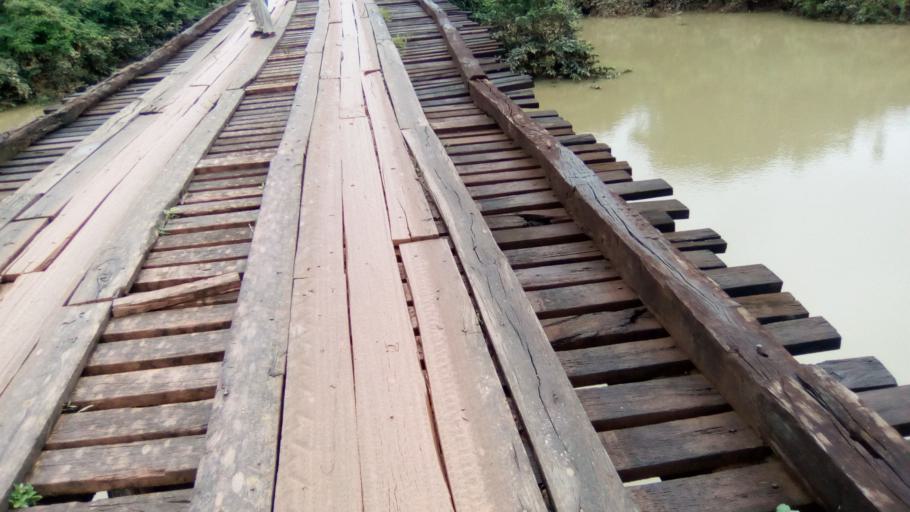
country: LA
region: Attapu
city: Attapu
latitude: 14.7100
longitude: 106.6584
